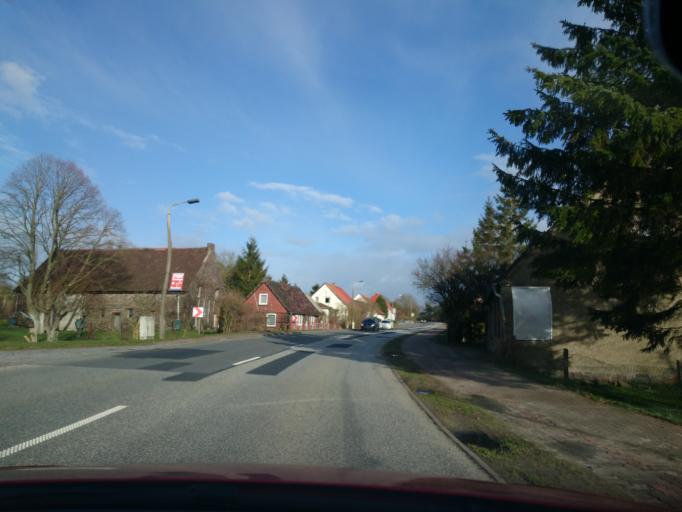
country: DE
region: Mecklenburg-Vorpommern
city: Barth
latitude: 54.2958
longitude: 12.7362
